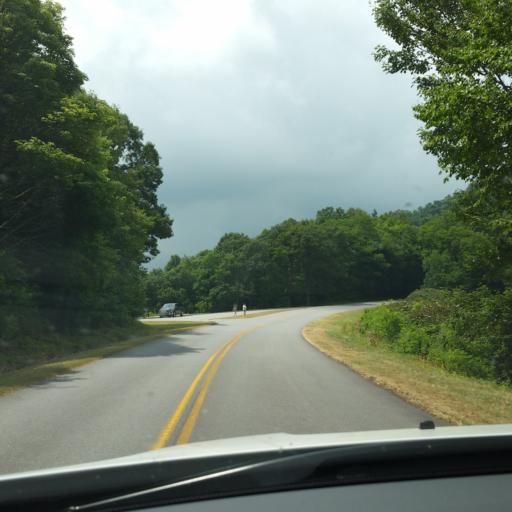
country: US
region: North Carolina
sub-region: Buncombe County
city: Bent Creek
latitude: 35.4437
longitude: -82.7195
